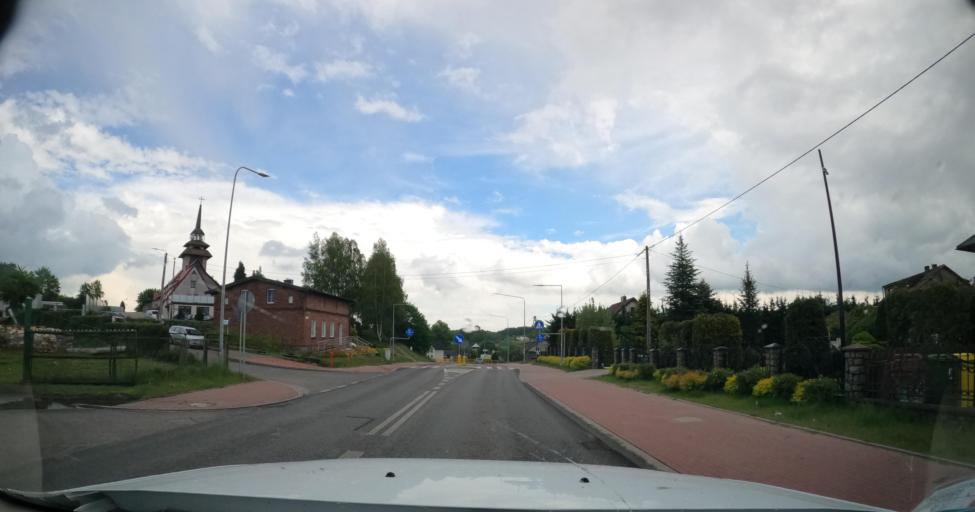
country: PL
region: Pomeranian Voivodeship
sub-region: Powiat kartuski
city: Chmielno
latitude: 54.3401
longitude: 18.0201
